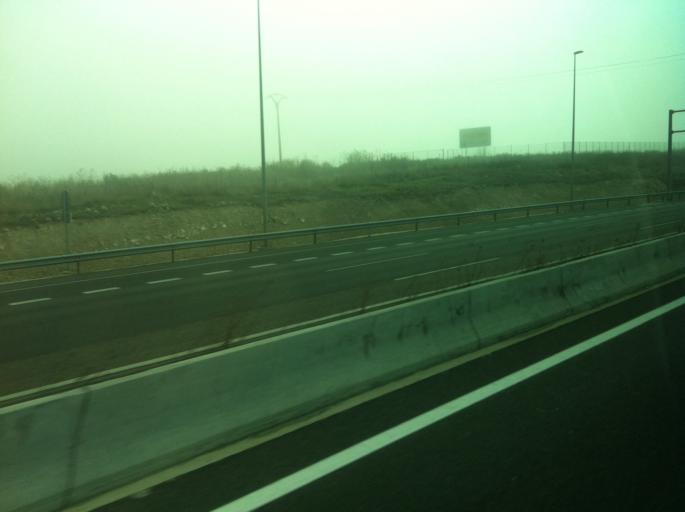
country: ES
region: Castille and Leon
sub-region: Provincia de Burgos
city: Saldana de Burgos
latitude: 42.2864
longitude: -3.7050
